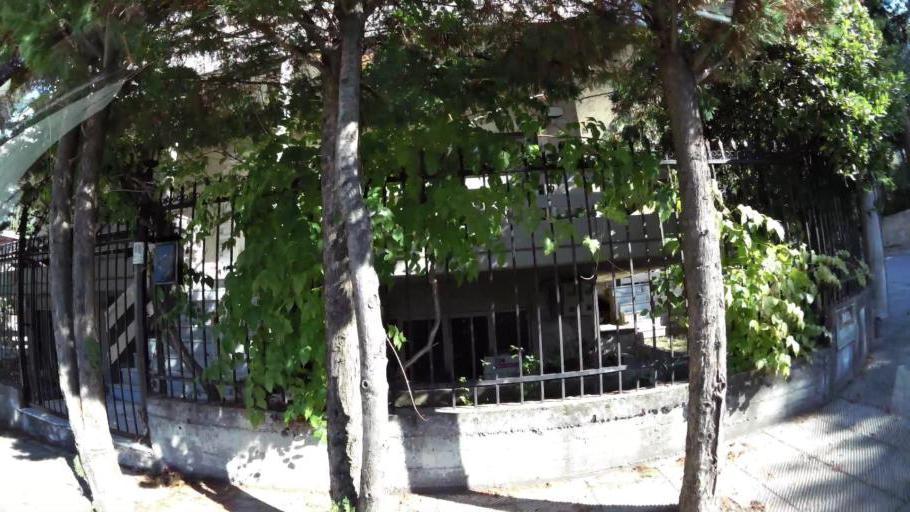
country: GR
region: Attica
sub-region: Nomarchia Anatolikis Attikis
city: Rodopoli
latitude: 38.1160
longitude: 23.8755
